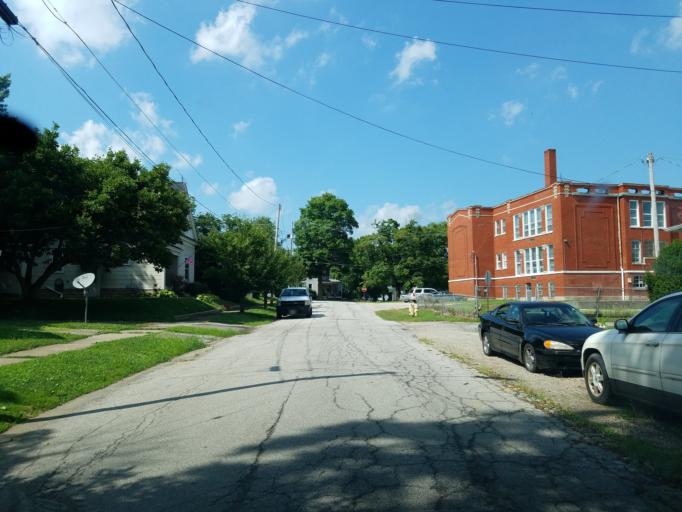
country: US
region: Ohio
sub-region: Ashland County
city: Ashland
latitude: 40.8718
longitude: -82.3213
